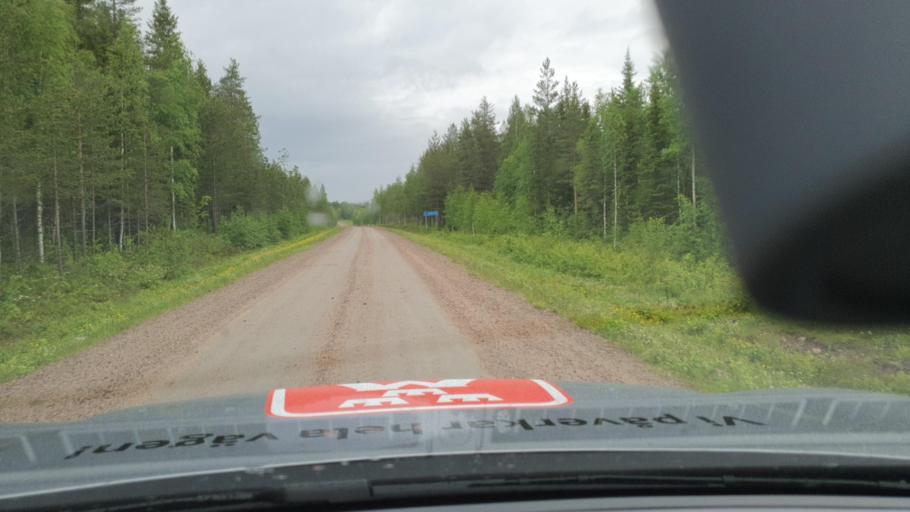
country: SE
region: Norrbotten
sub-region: Overkalix Kommun
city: OEverkalix
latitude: 66.6012
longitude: 22.7484
